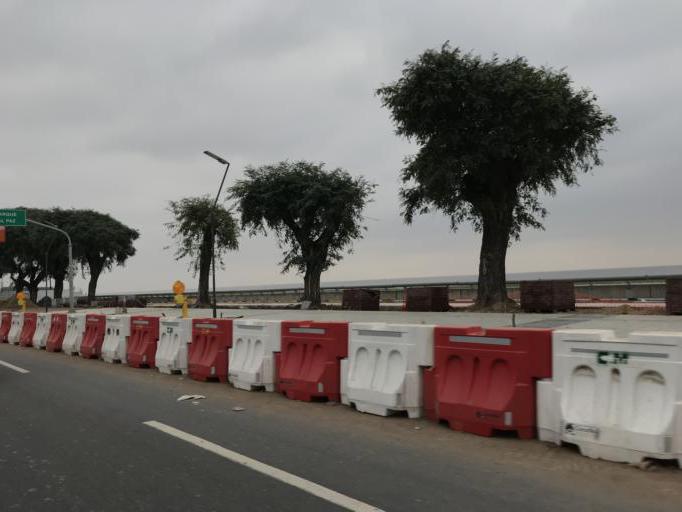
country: AR
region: Buenos Aires F.D.
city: Retiro
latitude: -34.5627
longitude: -58.4055
